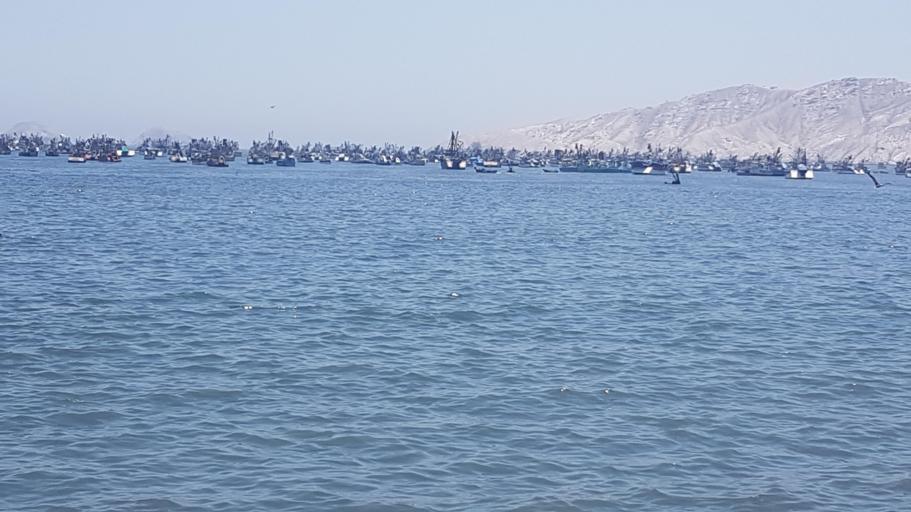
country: PE
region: Ancash
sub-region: Provincia de Santa
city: Chimbote
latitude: -9.0775
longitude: -78.5939
